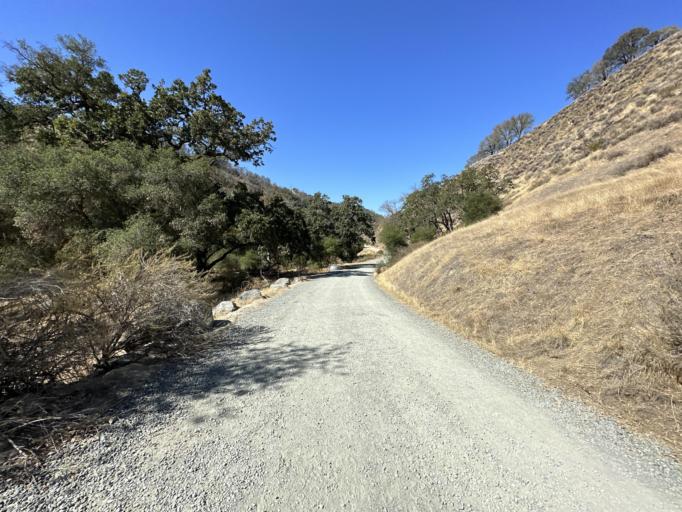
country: US
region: California
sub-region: Santa Clara County
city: Milpitas
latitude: 37.5041
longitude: -121.8239
